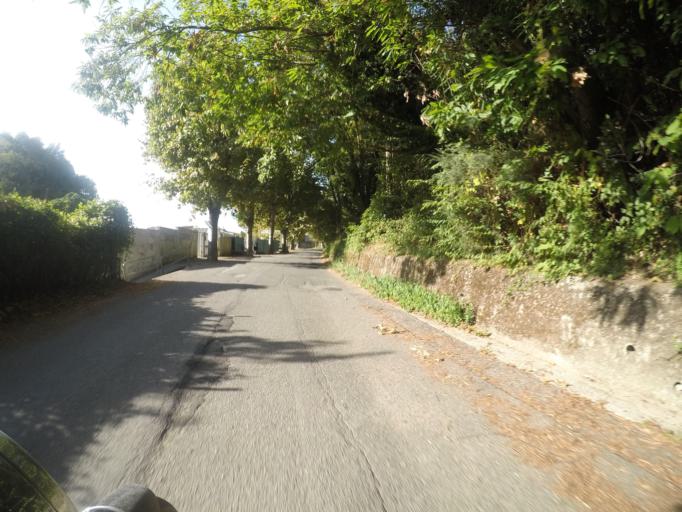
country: IT
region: Tuscany
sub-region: Provincia di Massa-Carrara
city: Massa
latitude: 44.0652
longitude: 10.1262
